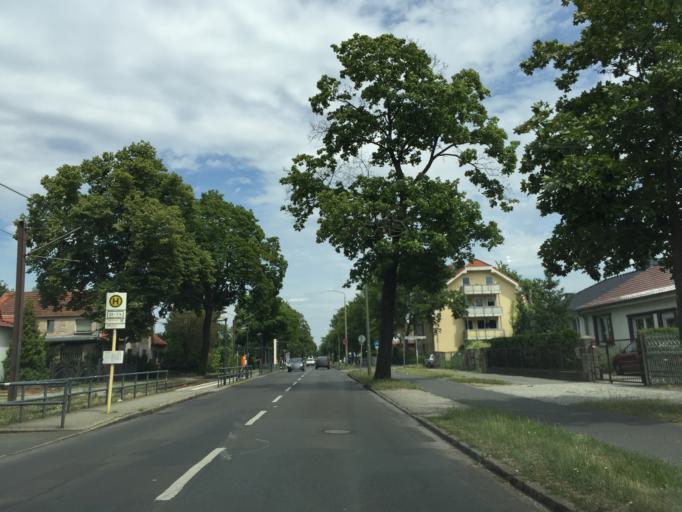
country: DE
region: Berlin
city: Mahlsdorf
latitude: 52.4883
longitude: 13.6057
